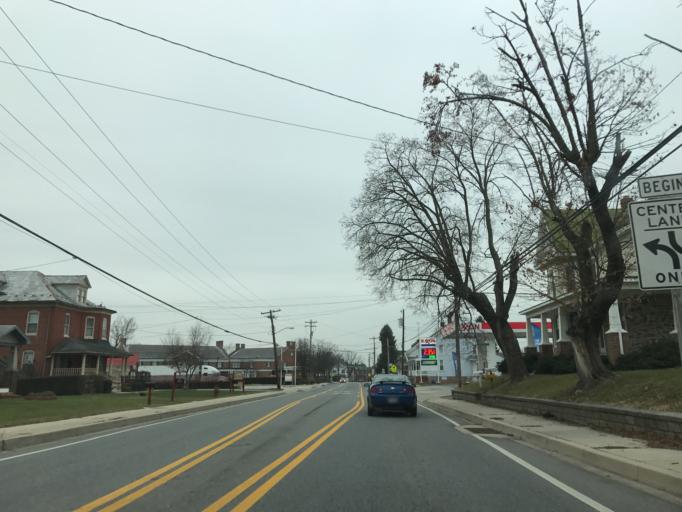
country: US
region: Maryland
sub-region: Carroll County
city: Taneytown
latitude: 39.6554
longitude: -77.1701
